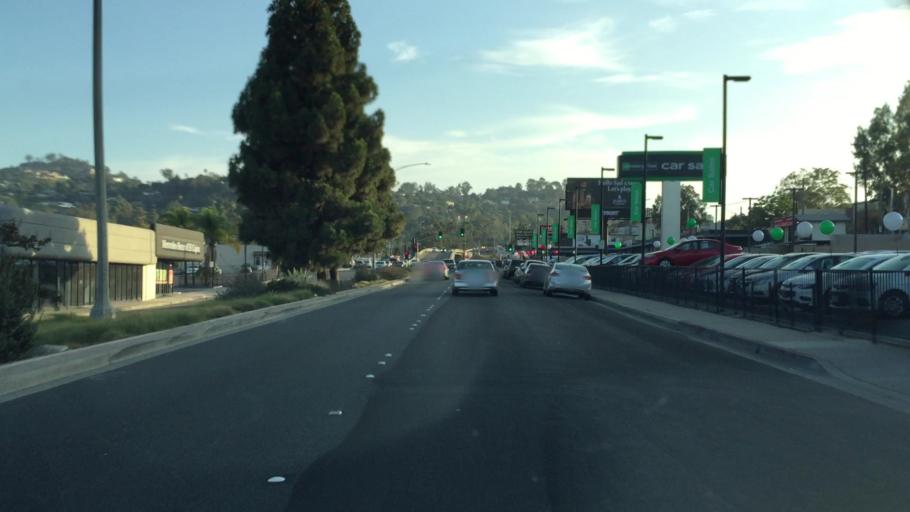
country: US
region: California
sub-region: San Diego County
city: El Cajon
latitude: 32.7857
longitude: -116.9769
